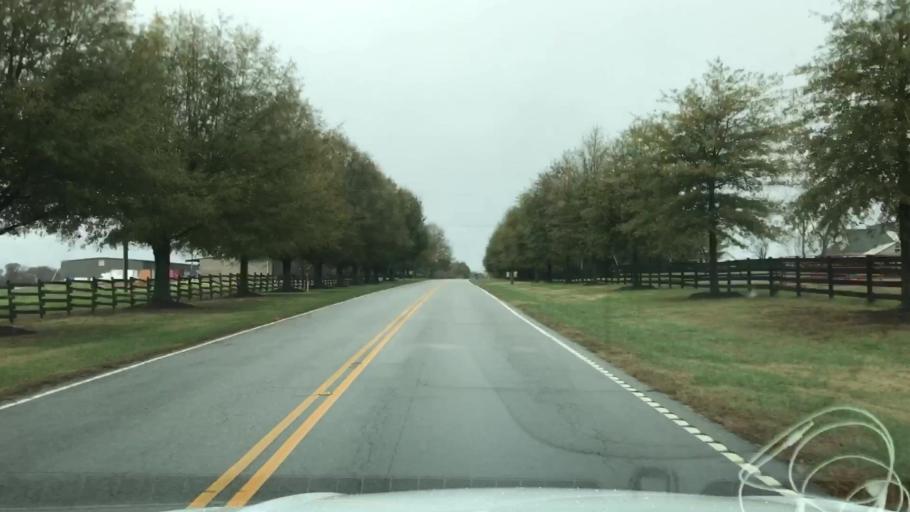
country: US
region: South Carolina
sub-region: Spartanburg County
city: Roebuck
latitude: 34.8115
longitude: -81.9226
